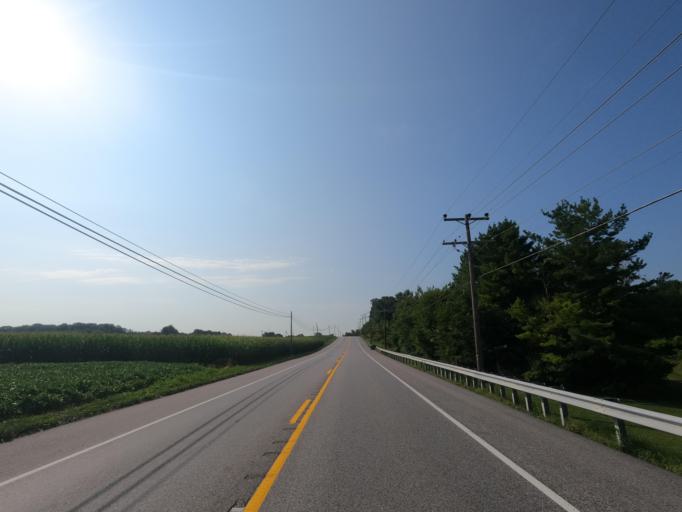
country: US
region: Maryland
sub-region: Carroll County
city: Westminster
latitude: 39.6286
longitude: -77.0004
